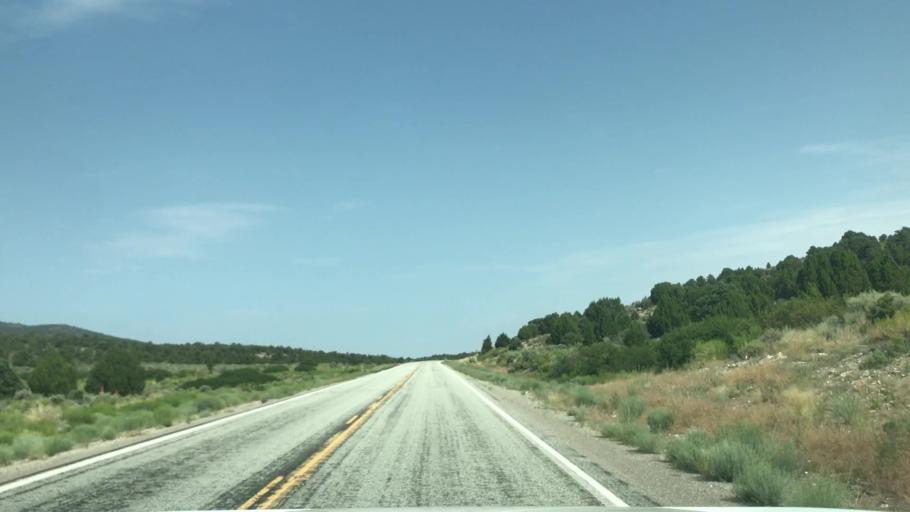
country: US
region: Nevada
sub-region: White Pine County
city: McGill
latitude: 39.1284
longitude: -114.3183
